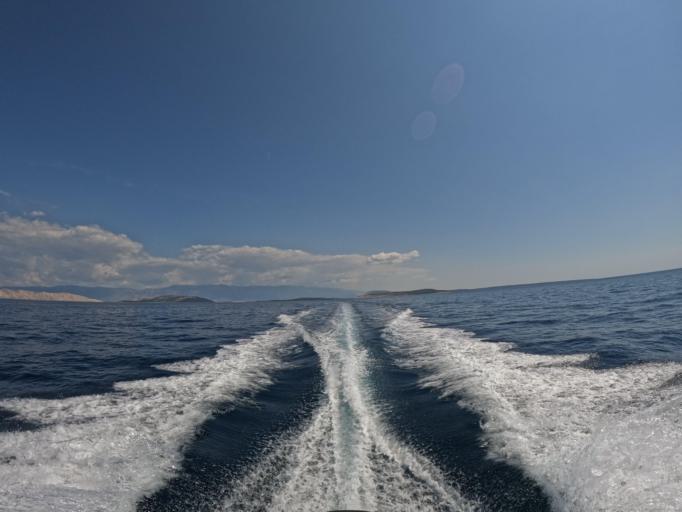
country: HR
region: Primorsko-Goranska
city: Lopar
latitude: 44.8814
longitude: 14.6500
